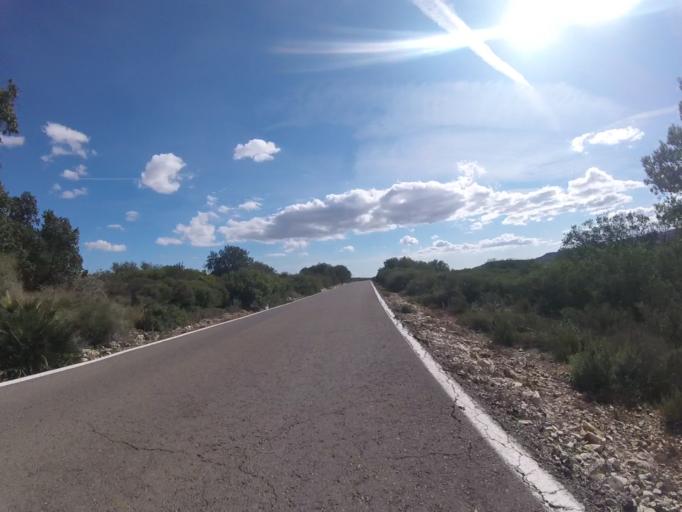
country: ES
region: Valencia
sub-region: Provincia de Castello
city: Albocasser
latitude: 40.3986
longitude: 0.0872
